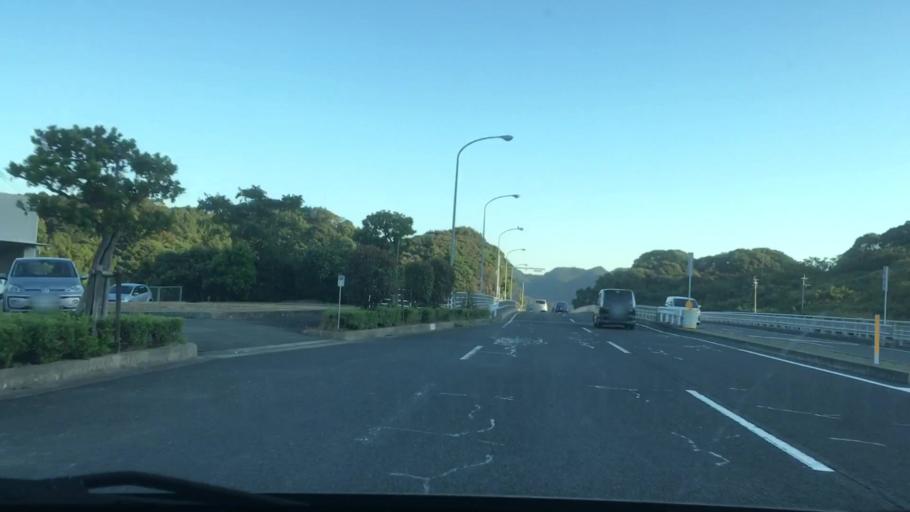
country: JP
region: Nagasaki
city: Sasebo
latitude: 33.1260
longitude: 129.7893
